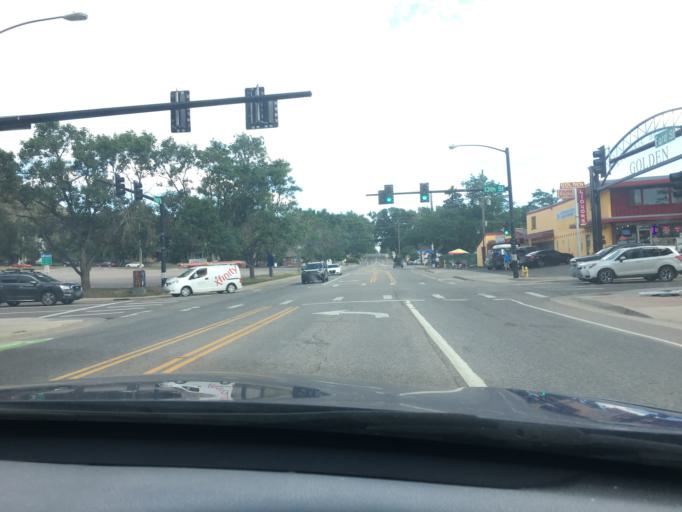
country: US
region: Colorado
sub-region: Jefferson County
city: Golden
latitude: 39.7560
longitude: -105.2187
